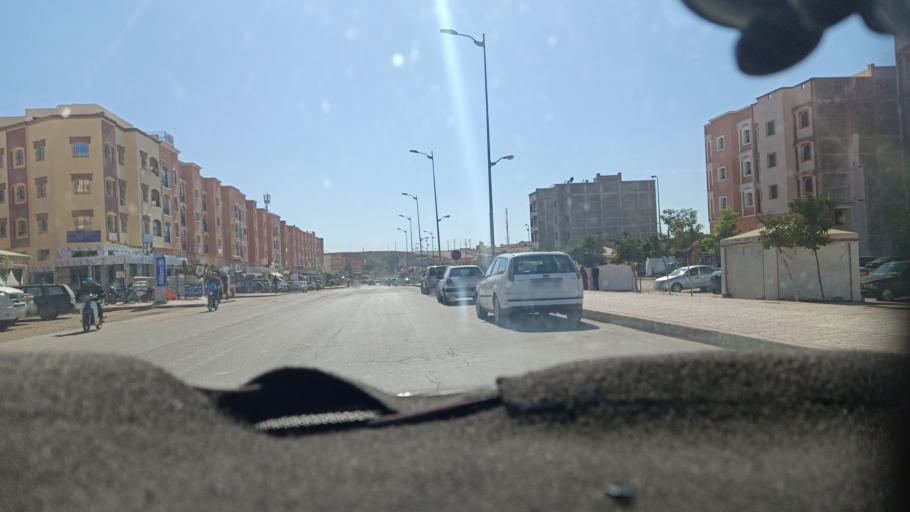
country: MA
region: Doukkala-Abda
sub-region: Safi
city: Youssoufia
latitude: 32.2412
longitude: -8.5381
